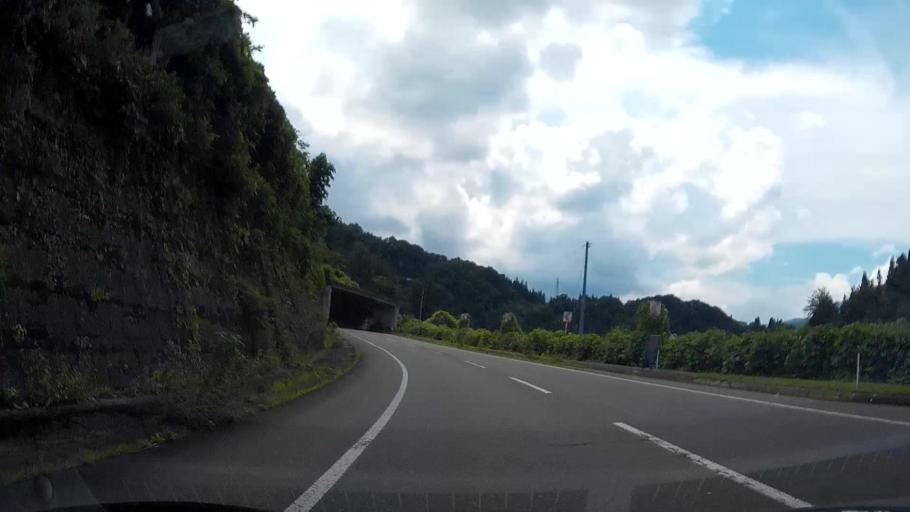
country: JP
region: Niigata
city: Tokamachi
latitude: 36.9938
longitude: 138.6113
